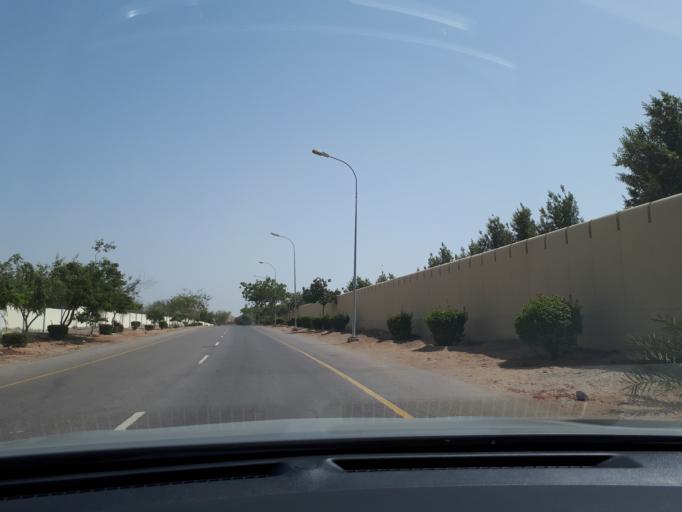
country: OM
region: Muhafazat Masqat
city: As Sib al Jadidah
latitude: 23.7063
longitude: 58.0744
